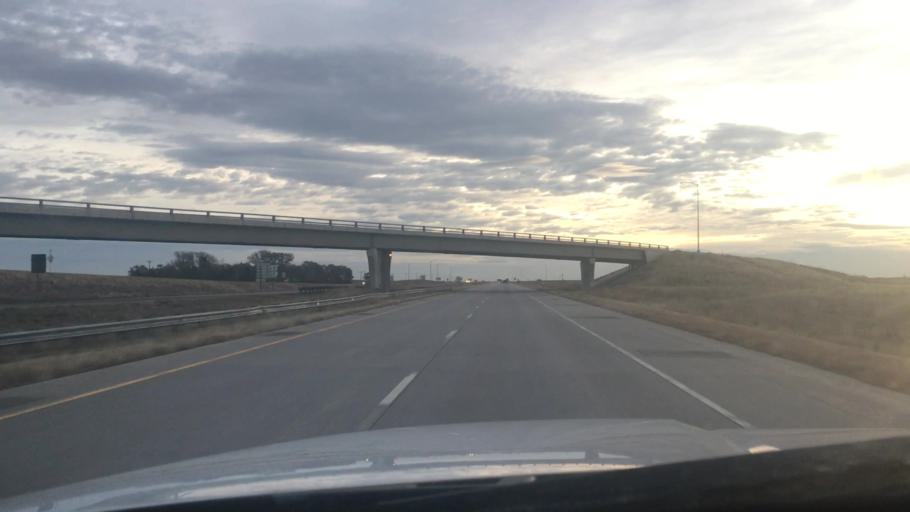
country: US
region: Colorado
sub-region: Morgan County
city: Fort Morgan
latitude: 40.2460
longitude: -104.0538
